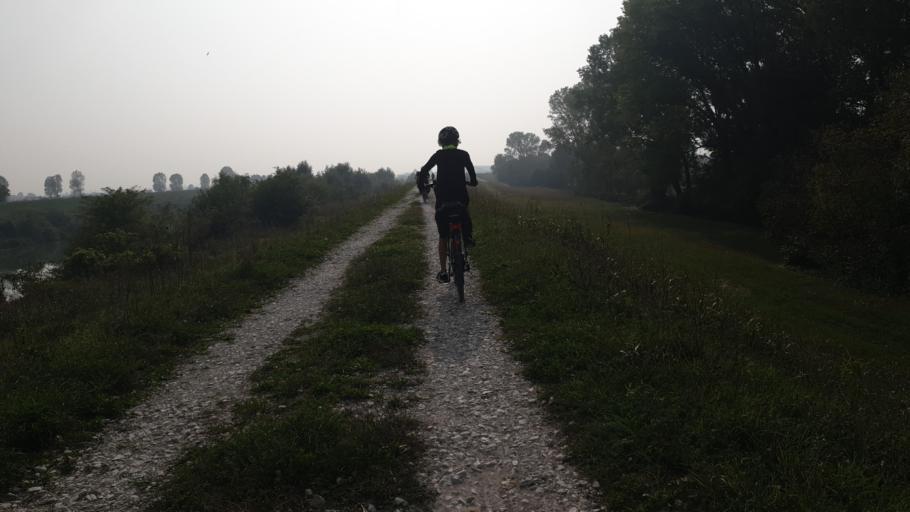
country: IT
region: Veneto
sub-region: Provincia di Padova
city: Corte
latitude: 45.3222
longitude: 12.0696
